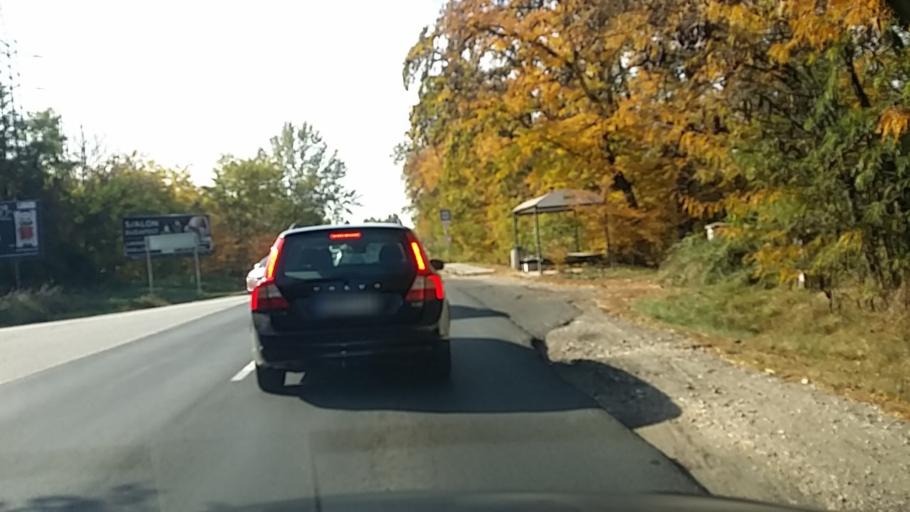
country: HU
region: Pest
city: Fot
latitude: 47.5867
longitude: 19.1581
